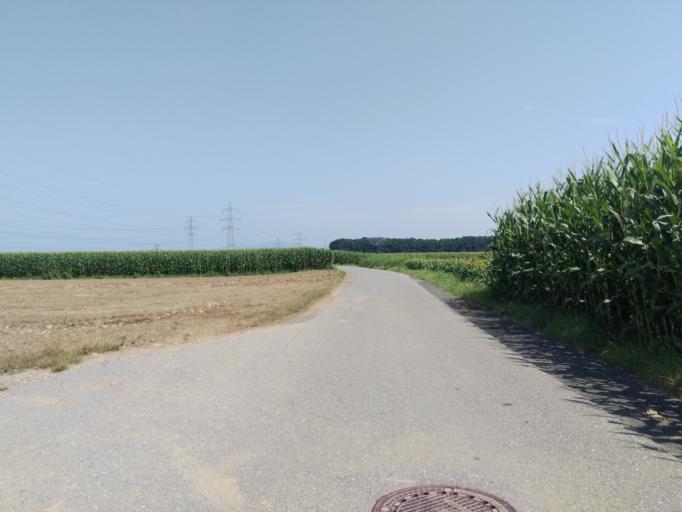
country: AT
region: Styria
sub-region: Politischer Bezirk Graz-Umgebung
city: Werndorf
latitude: 46.9300
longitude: 15.4899
